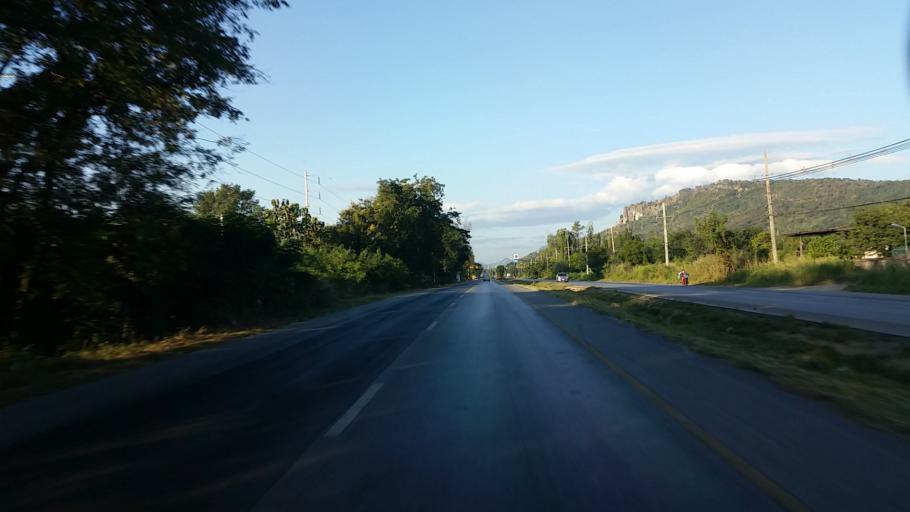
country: TH
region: Lop Buri
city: Chai Badan
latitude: 15.2054
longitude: 101.1019
